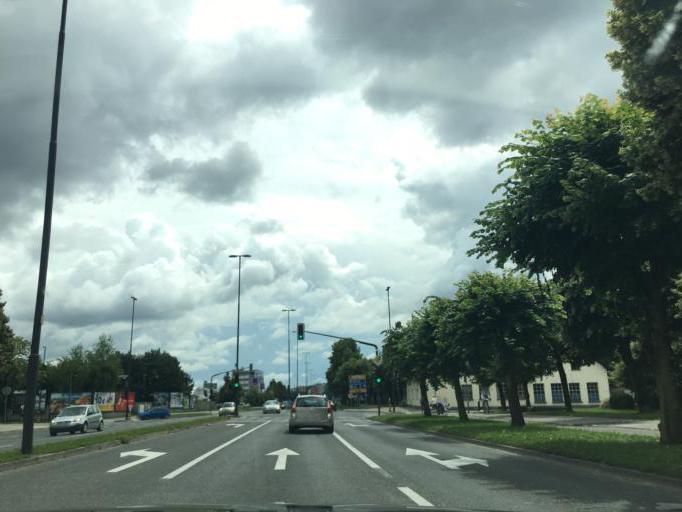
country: SI
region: Ljubljana
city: Ljubljana
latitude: 46.0836
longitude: 14.4777
